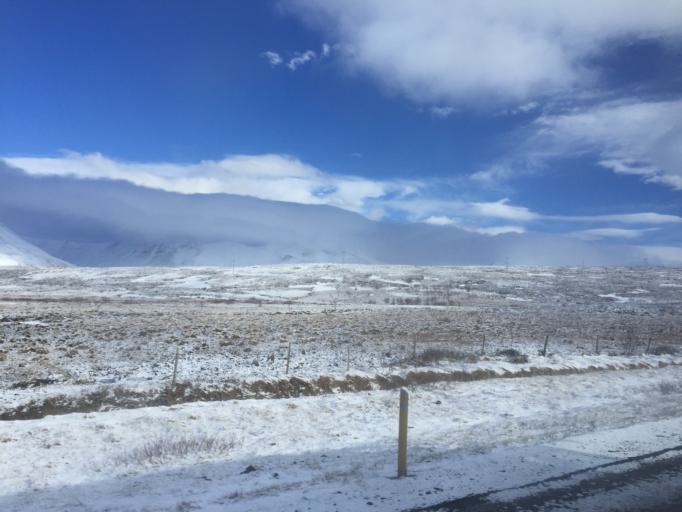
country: IS
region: Capital Region
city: Mosfellsbaer
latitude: 64.1852
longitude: -21.5614
